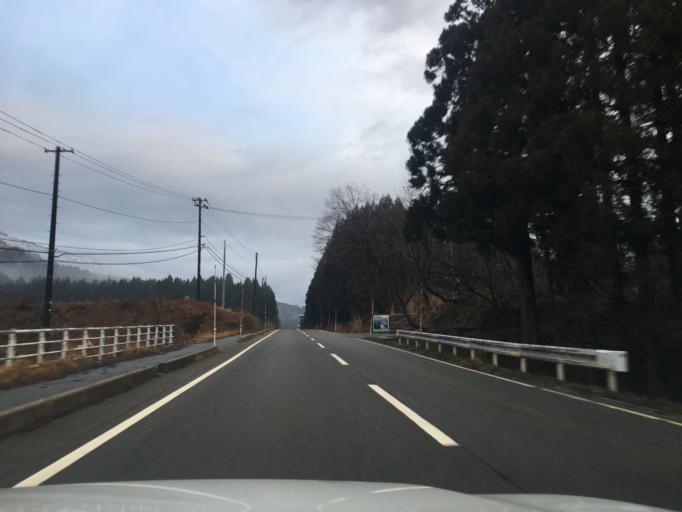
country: JP
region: Niigata
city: Murakami
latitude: 38.3631
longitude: 139.5527
